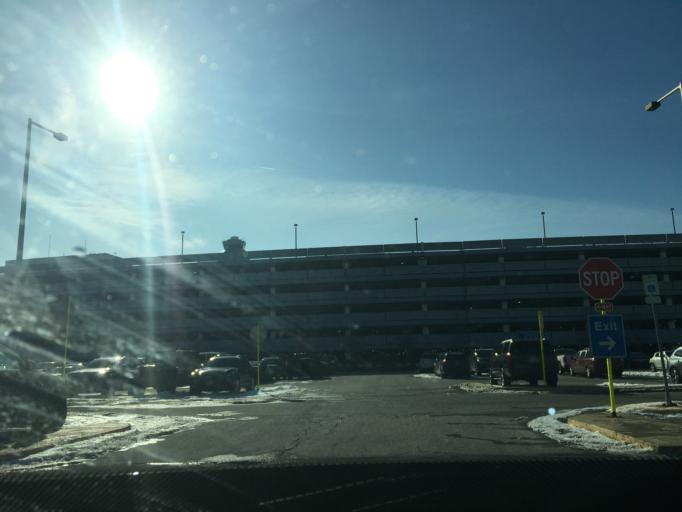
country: US
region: Illinois
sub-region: Cook County
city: Rosemont
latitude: 41.9790
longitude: -87.9013
